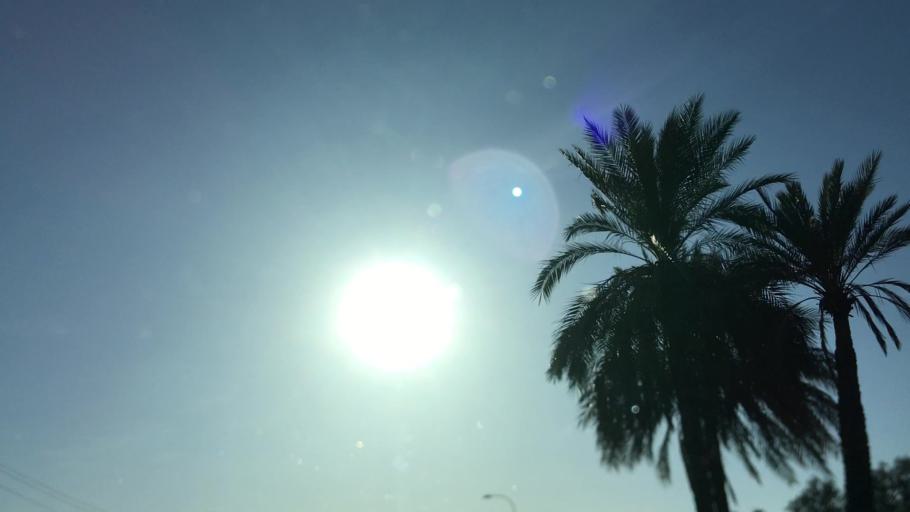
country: US
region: Arizona
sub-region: Maricopa County
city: Peoria
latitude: 33.5817
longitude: -112.2064
